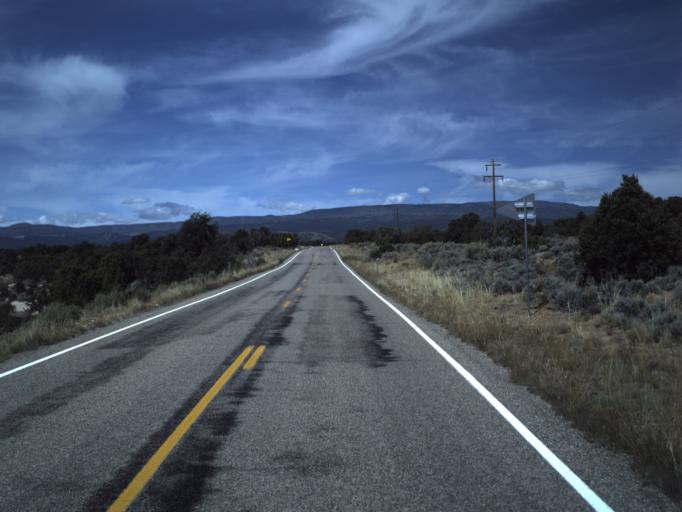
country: US
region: Utah
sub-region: Wayne County
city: Loa
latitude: 37.8569
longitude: -111.4345
